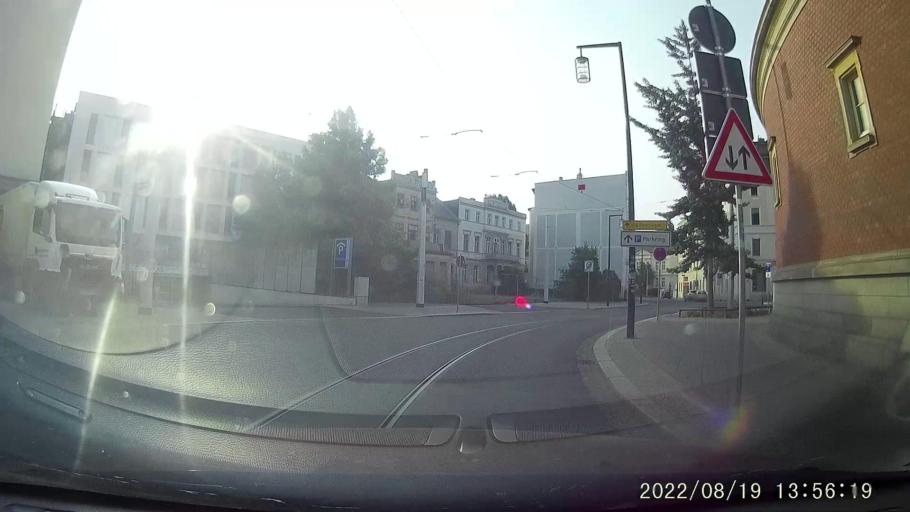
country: DE
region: Saxony
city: Goerlitz
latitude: 51.1544
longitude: 14.9651
